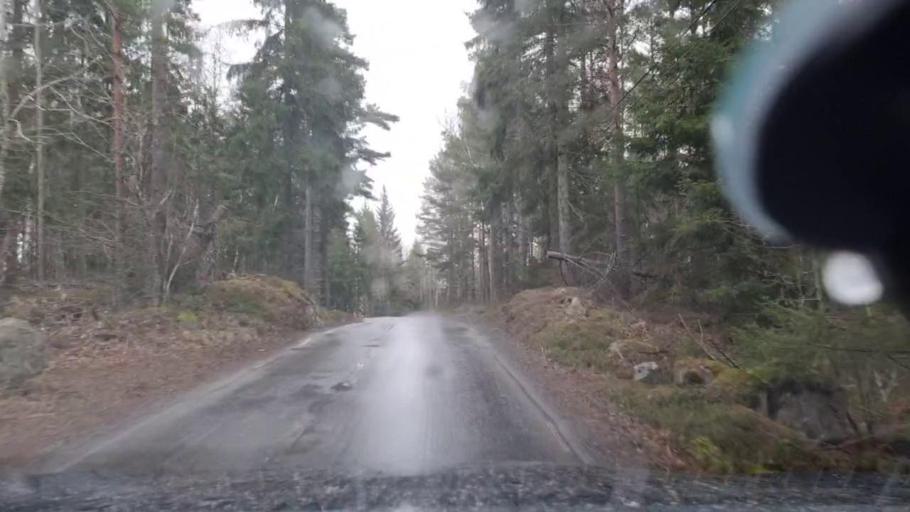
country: SE
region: Stockholm
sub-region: Vallentuna Kommun
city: Vallentuna
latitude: 59.5111
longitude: 18.0091
